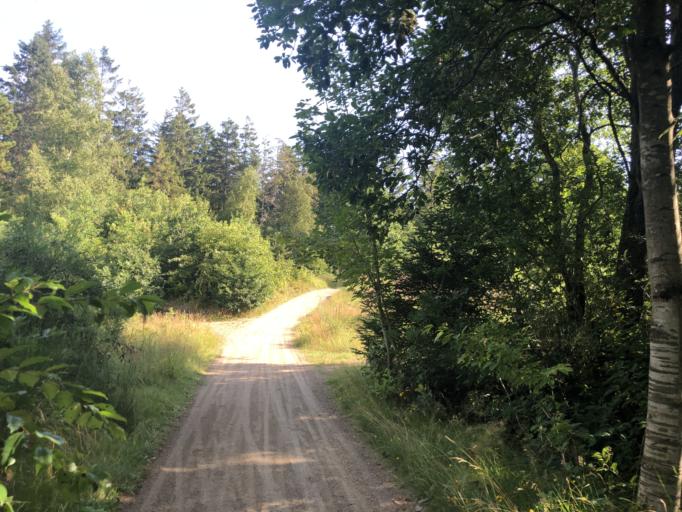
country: DK
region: Central Jutland
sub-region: Holstebro Kommune
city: Ulfborg
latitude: 56.3295
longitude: 8.4103
